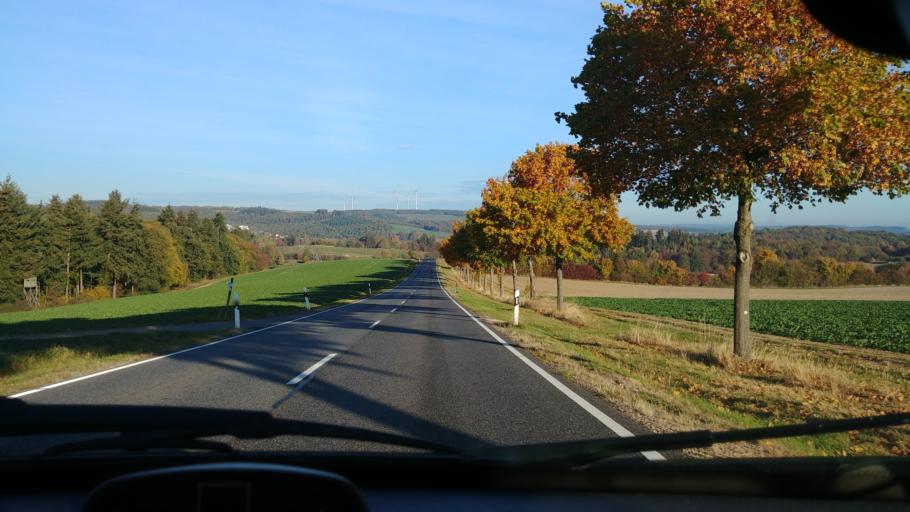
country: DE
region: Hesse
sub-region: Regierungsbezirk Darmstadt
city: Bad Schwalbach
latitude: 50.1273
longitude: 8.0799
